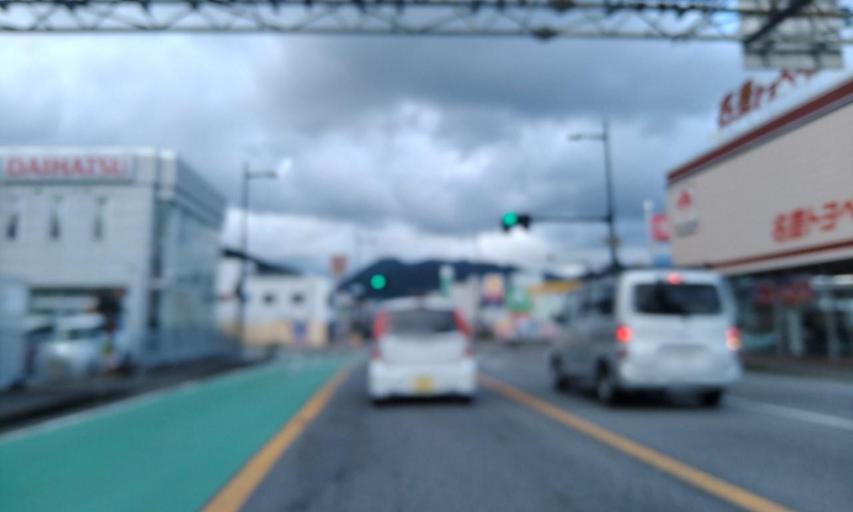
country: JP
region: Wakayama
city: Shingu
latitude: 33.7187
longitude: 135.9870
